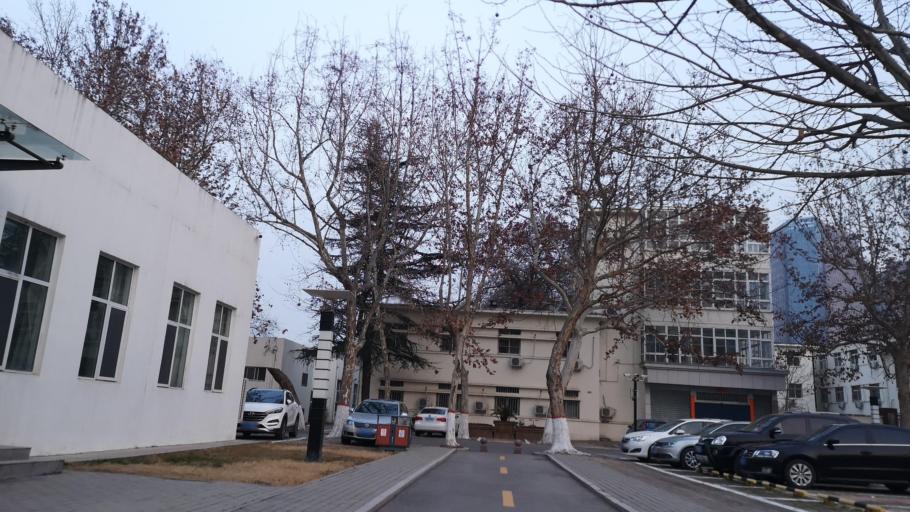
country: CN
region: Henan Sheng
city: Zhongyuanlu
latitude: 35.7767
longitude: 115.0760
